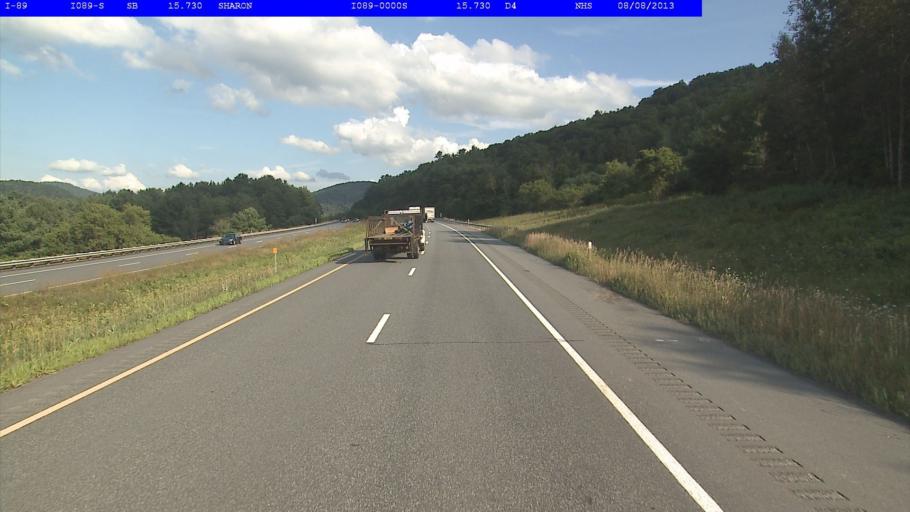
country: US
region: Vermont
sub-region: Windsor County
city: Woodstock
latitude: 43.7874
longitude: -72.4955
